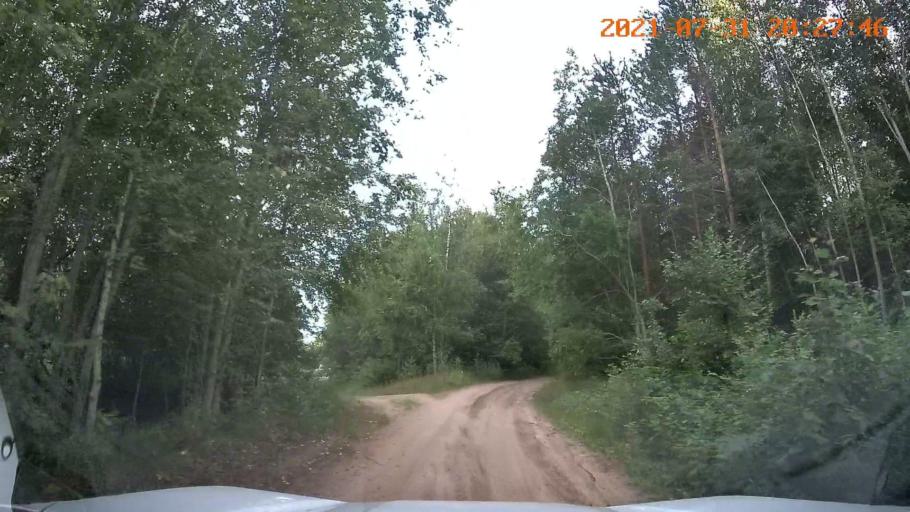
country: RU
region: Republic of Karelia
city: Pudozh
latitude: 61.6657
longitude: 36.3034
